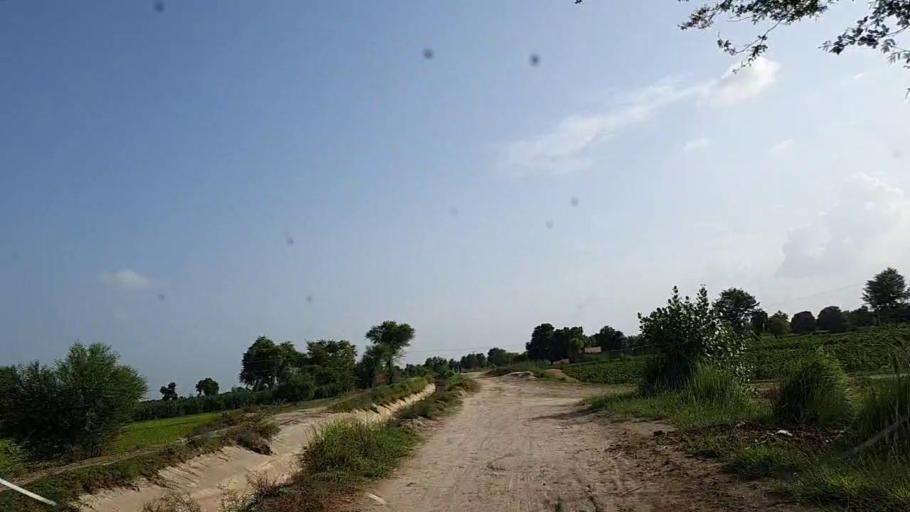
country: PK
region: Sindh
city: Bhiria
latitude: 26.8638
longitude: 68.2526
